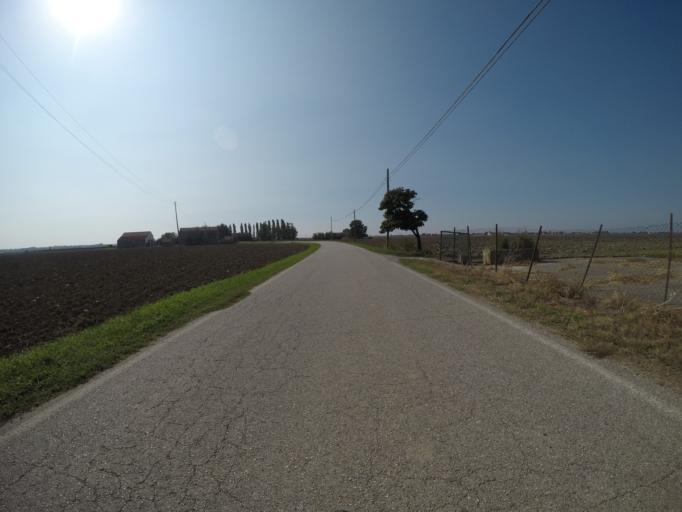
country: IT
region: Veneto
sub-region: Provincia di Rovigo
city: Polesella
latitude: 44.9790
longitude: 11.7249
